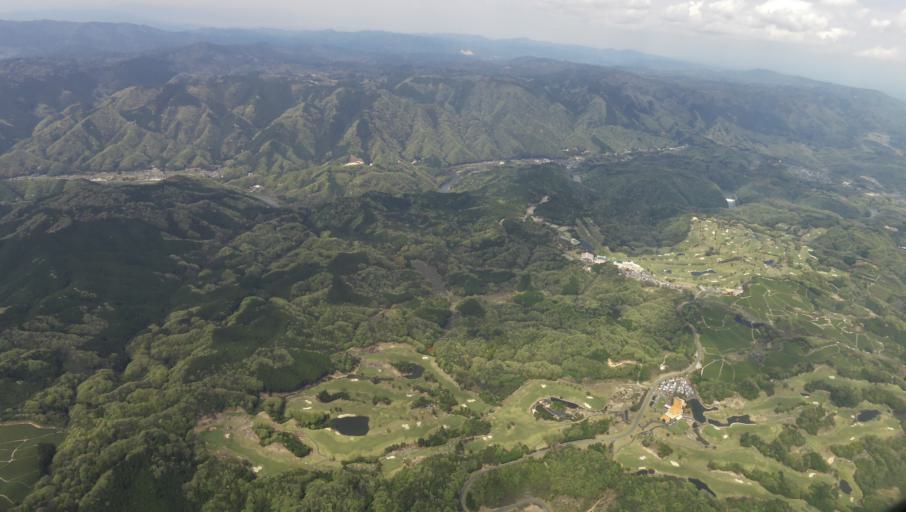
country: JP
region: Mie
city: Ueno-ebisumachi
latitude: 34.7341
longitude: 135.9764
